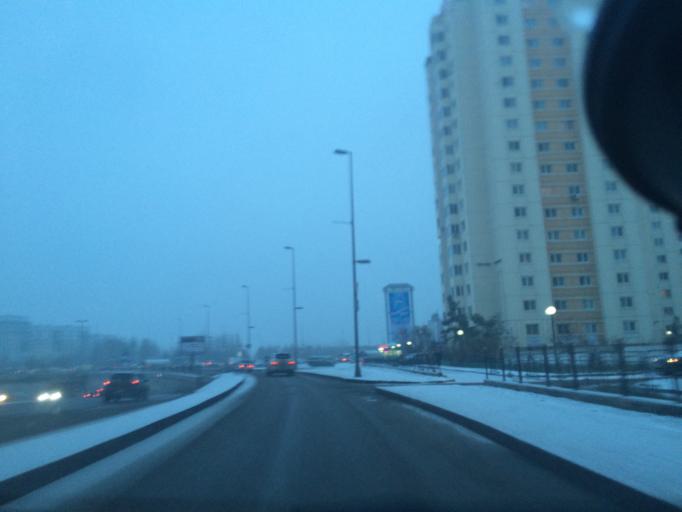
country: KZ
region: Astana Qalasy
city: Astana
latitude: 51.1555
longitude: 71.4298
